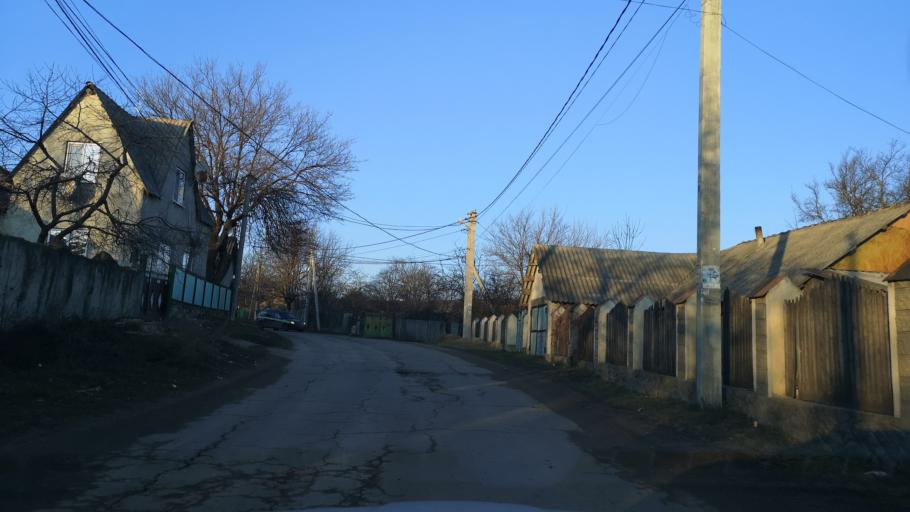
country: MD
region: Orhei
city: Orhei
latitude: 47.3591
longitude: 28.6910
